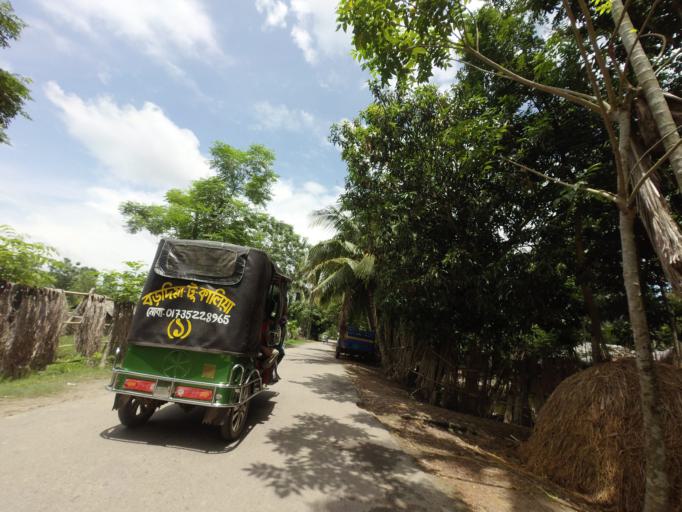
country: BD
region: Khulna
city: Kalia
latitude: 23.0403
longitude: 89.6369
